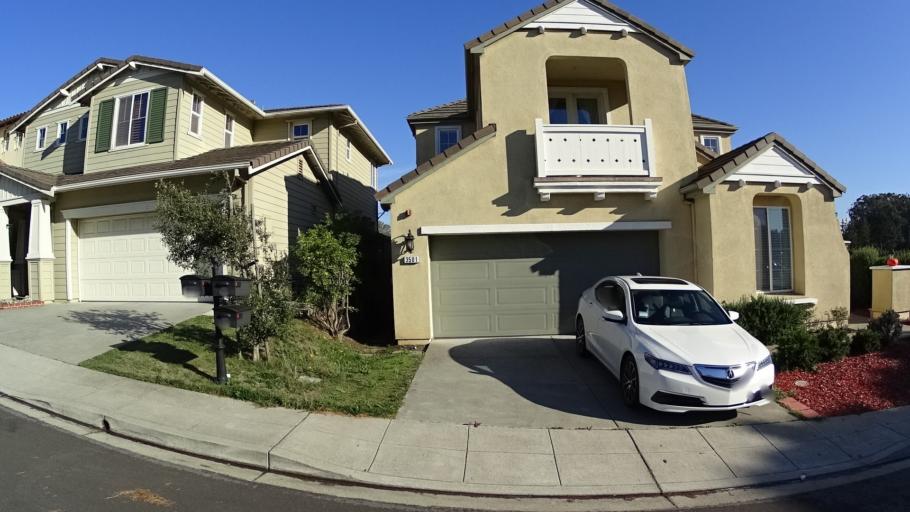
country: US
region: California
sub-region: San Mateo County
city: Pacifica
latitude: 37.6321
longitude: -122.4633
